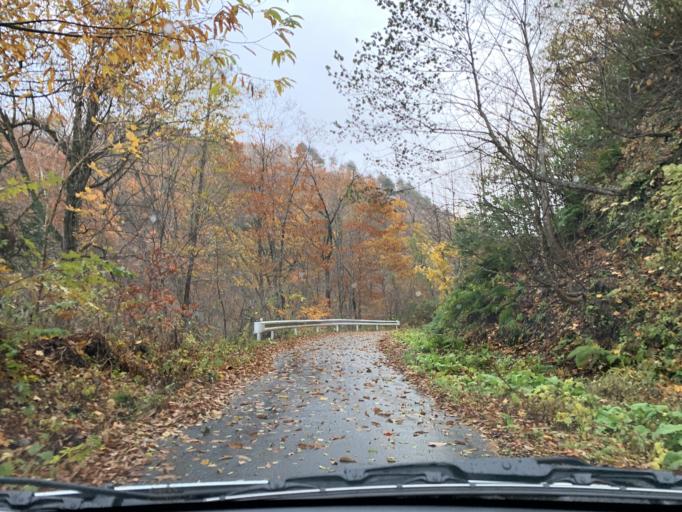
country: JP
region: Iwate
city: Mizusawa
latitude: 39.0982
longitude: 140.9379
